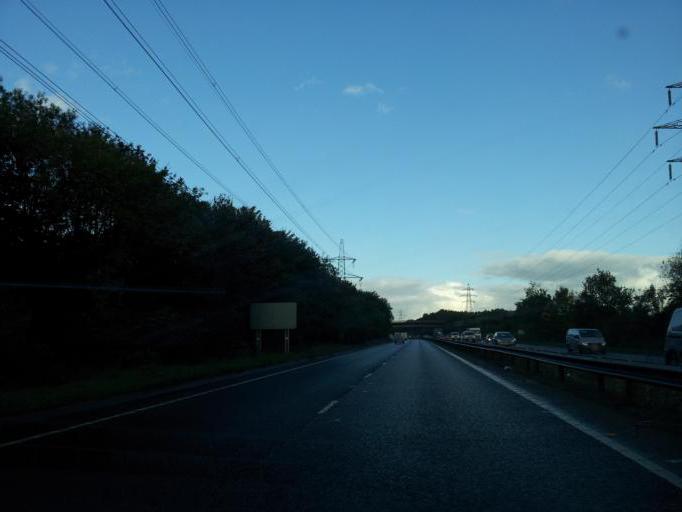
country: GB
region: England
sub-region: Norfolk
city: Cringleford
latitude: 52.5924
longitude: 1.2447
